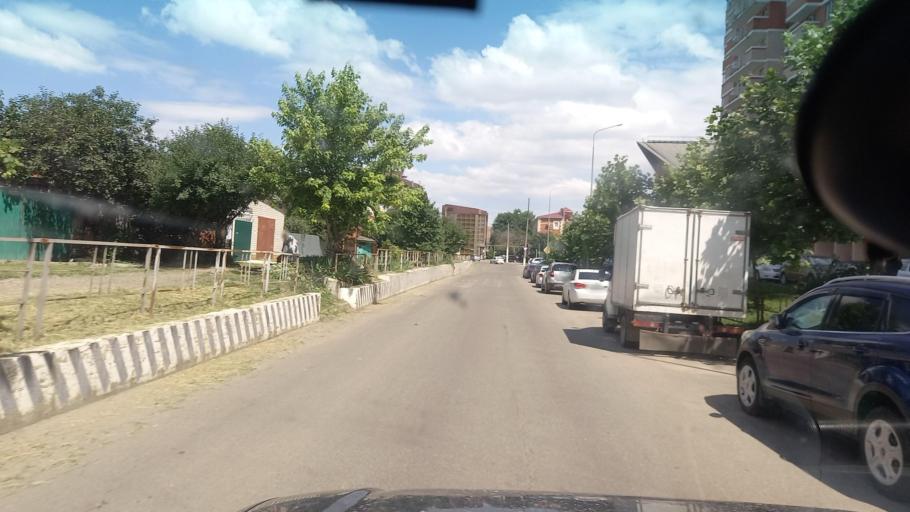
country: RU
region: Krasnodarskiy
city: Krasnodar
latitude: 45.0402
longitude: 38.9515
